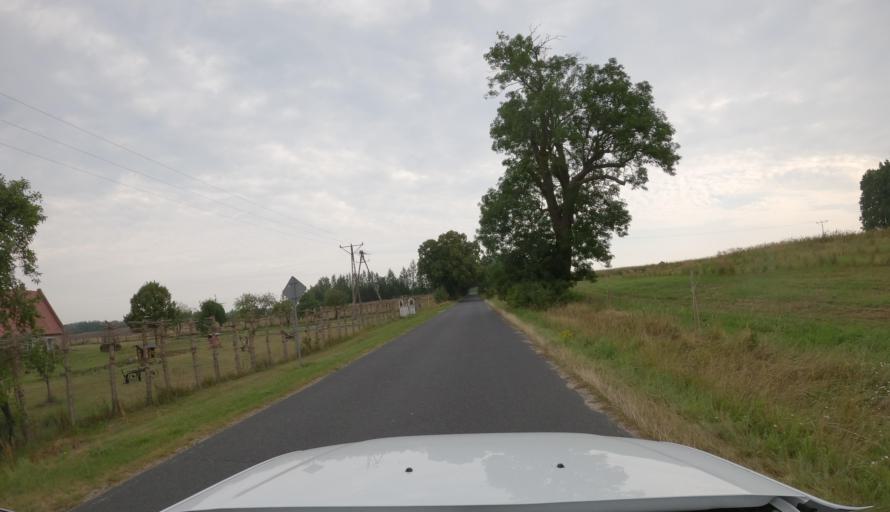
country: PL
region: West Pomeranian Voivodeship
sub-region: Powiat lobeski
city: Lobez
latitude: 53.7825
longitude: 15.6000
